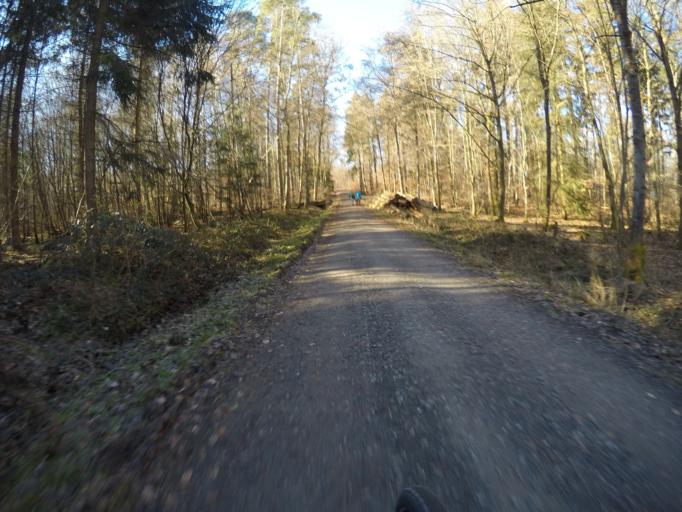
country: DE
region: Baden-Wuerttemberg
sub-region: Regierungsbezirk Stuttgart
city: Sindelfingen
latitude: 48.6932
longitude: 9.0351
